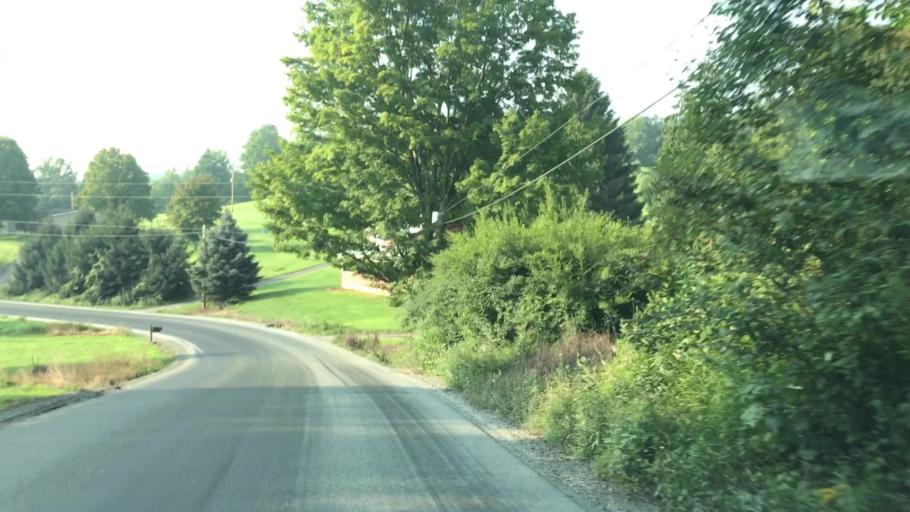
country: US
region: Pennsylvania
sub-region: Wyoming County
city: Factoryville
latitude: 41.6593
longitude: -75.8026
